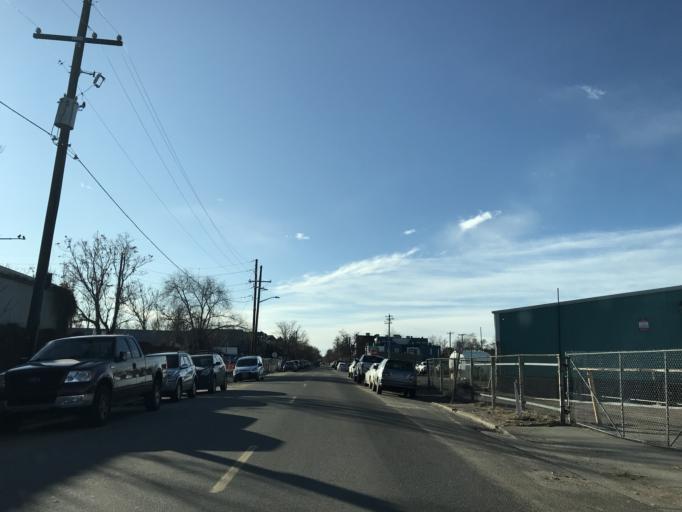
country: US
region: Colorado
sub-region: Denver County
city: Denver
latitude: 39.7720
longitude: -104.9684
